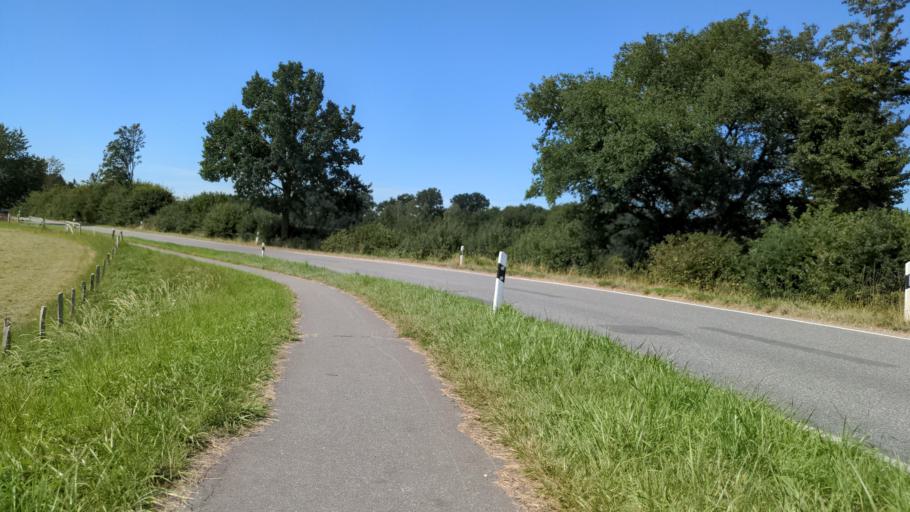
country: DE
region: Schleswig-Holstein
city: Grebin
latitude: 54.1961
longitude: 10.5093
